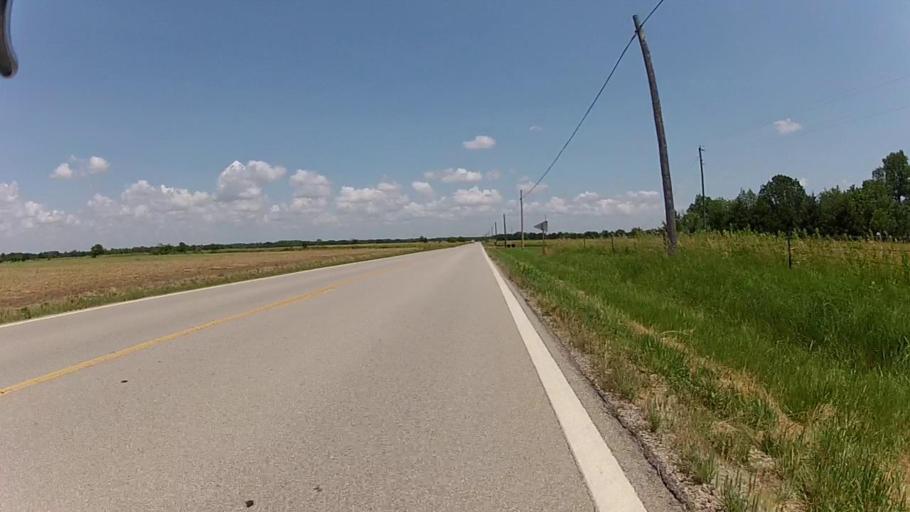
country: US
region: Kansas
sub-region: Labette County
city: Altamont
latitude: 37.1924
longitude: -95.4288
